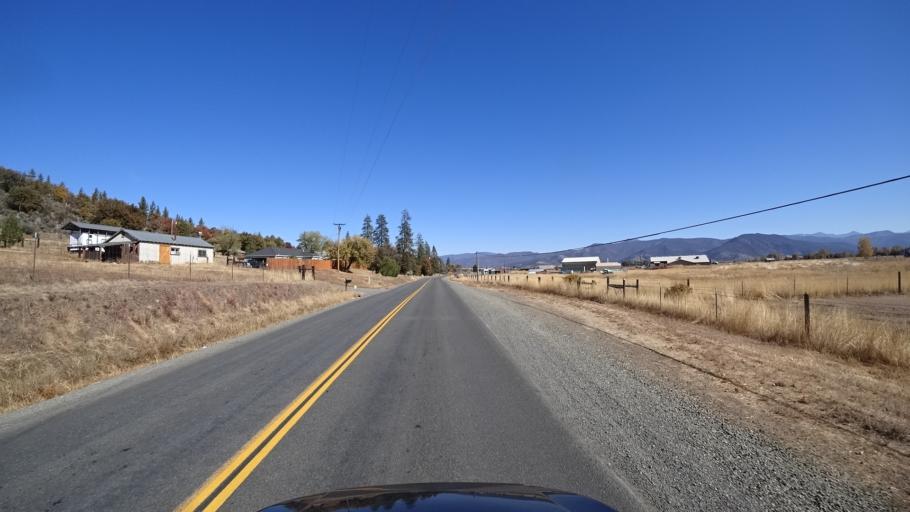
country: US
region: California
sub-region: Siskiyou County
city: Yreka
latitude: 41.5518
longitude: -122.9048
